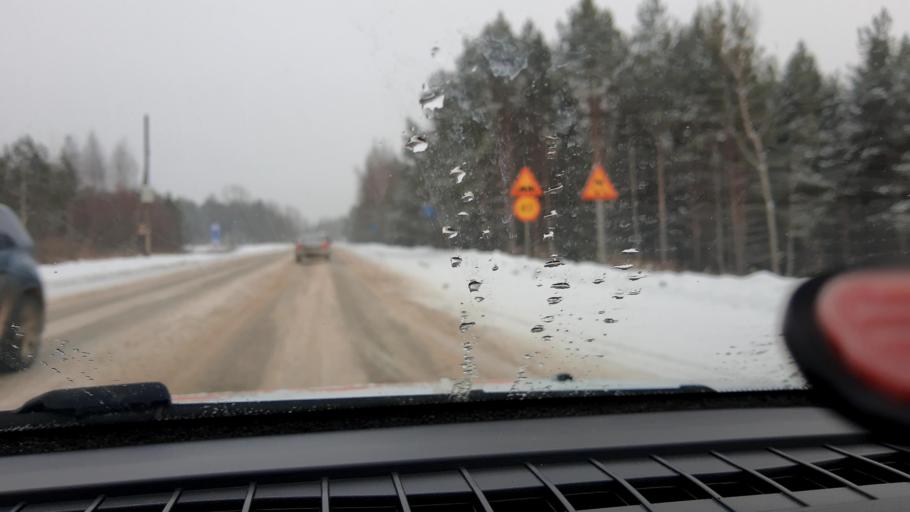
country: RU
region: Nizjnij Novgorod
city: Bor
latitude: 56.3255
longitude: 44.1378
